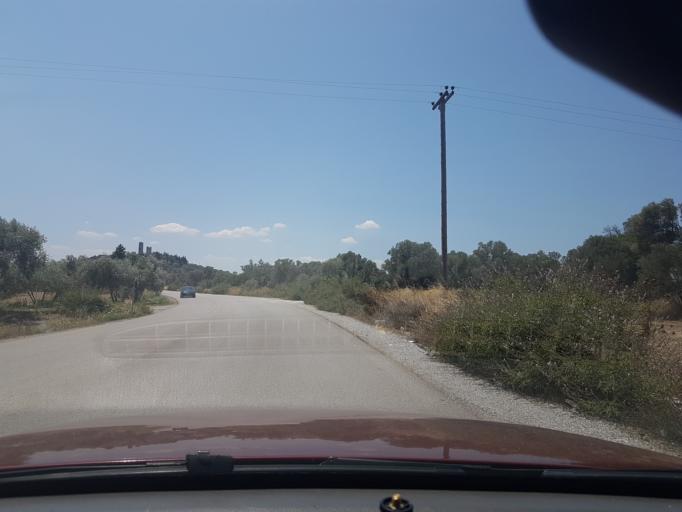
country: GR
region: Central Greece
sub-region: Nomos Evvoias
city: Afration
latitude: 38.4514
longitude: 23.6768
